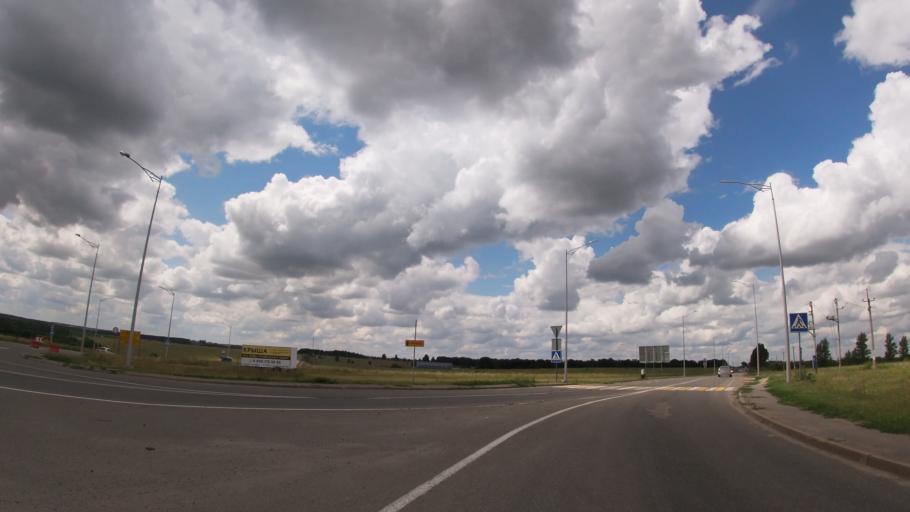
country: RU
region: Belgorod
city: Mayskiy
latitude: 50.5267
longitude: 36.5185
